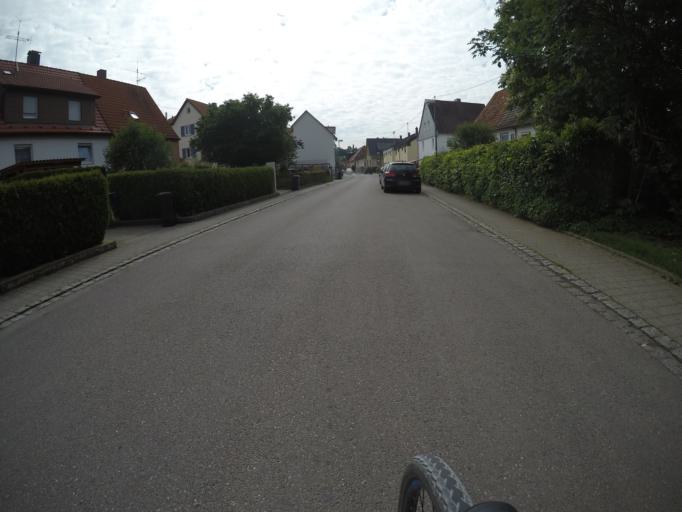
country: DE
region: Baden-Wuerttemberg
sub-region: Regierungsbezirk Stuttgart
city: Oberboihingen
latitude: 48.6494
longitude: 9.3614
